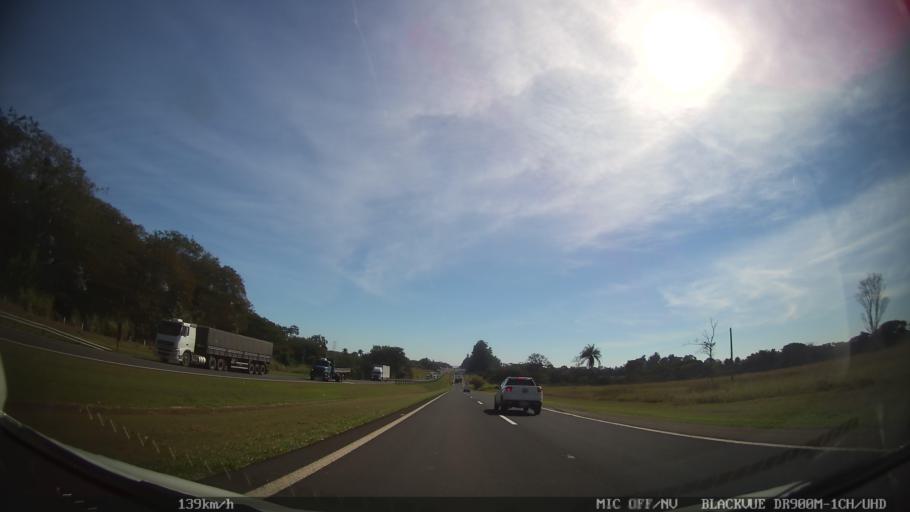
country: BR
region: Sao Paulo
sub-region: Pirassununga
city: Pirassununga
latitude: -21.9686
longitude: -47.4558
